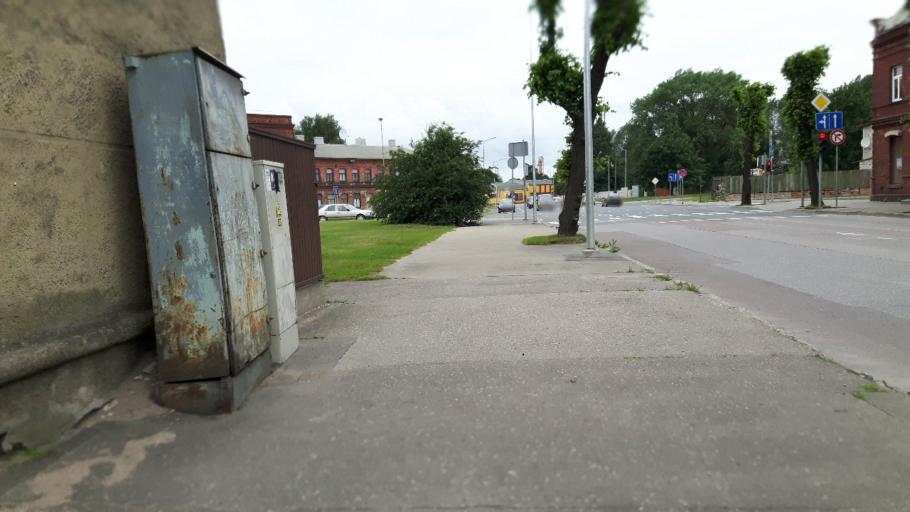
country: LV
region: Liepaja
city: Liepaja
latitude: 56.5203
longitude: 21.0071
